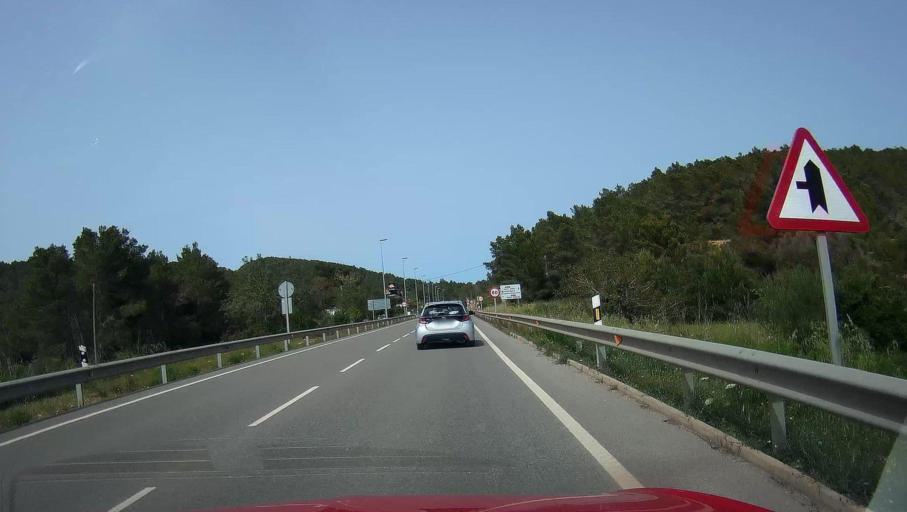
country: ES
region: Balearic Islands
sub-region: Illes Balears
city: Sant Joan de Labritja
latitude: 39.0689
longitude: 1.4956
